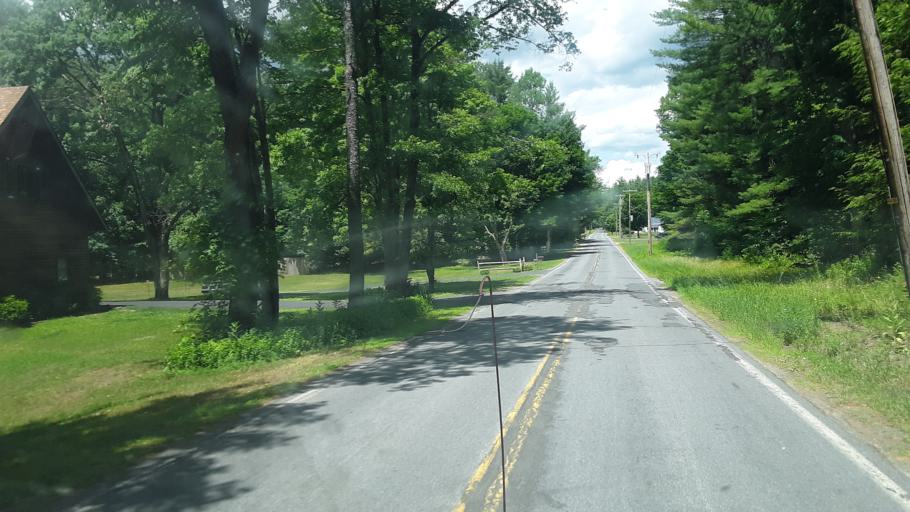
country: US
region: New York
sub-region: Oneida County
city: Rome
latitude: 43.2429
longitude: -75.5973
